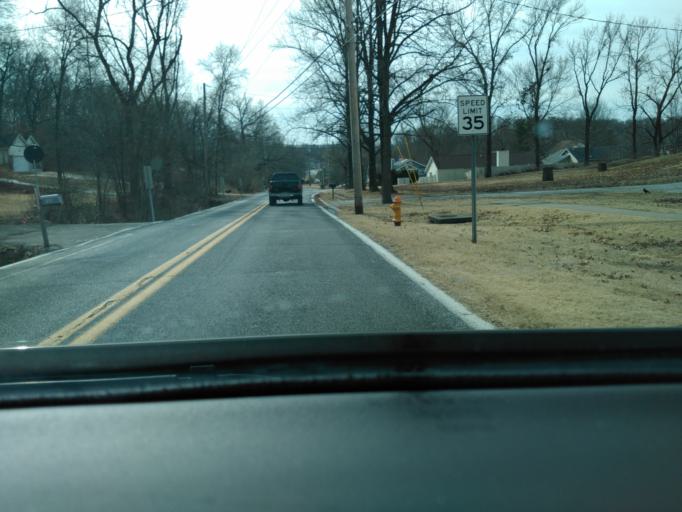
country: US
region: Missouri
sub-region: Saint Louis County
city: Valley Park
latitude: 38.5576
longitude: -90.5111
